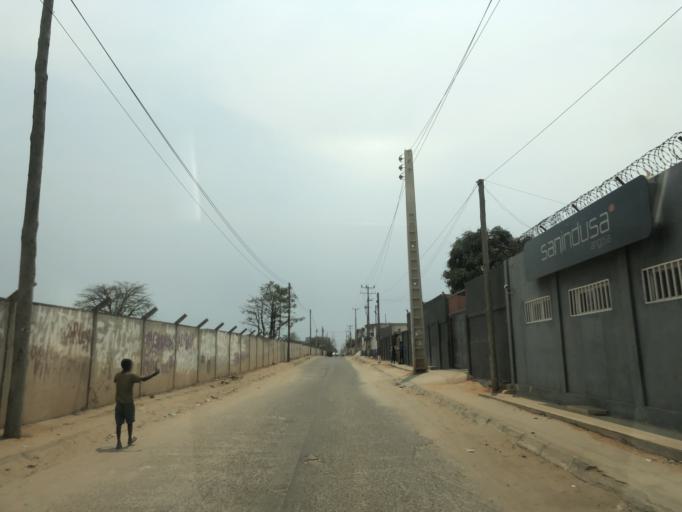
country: AO
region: Luanda
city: Luanda
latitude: -8.8888
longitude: 13.1948
